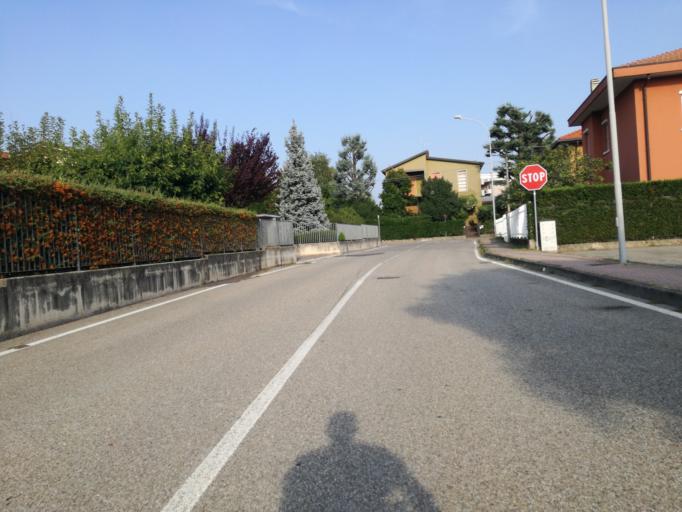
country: IT
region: Lombardy
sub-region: Provincia di Lecco
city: Paderno d'Adda
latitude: 45.6763
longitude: 9.4458
